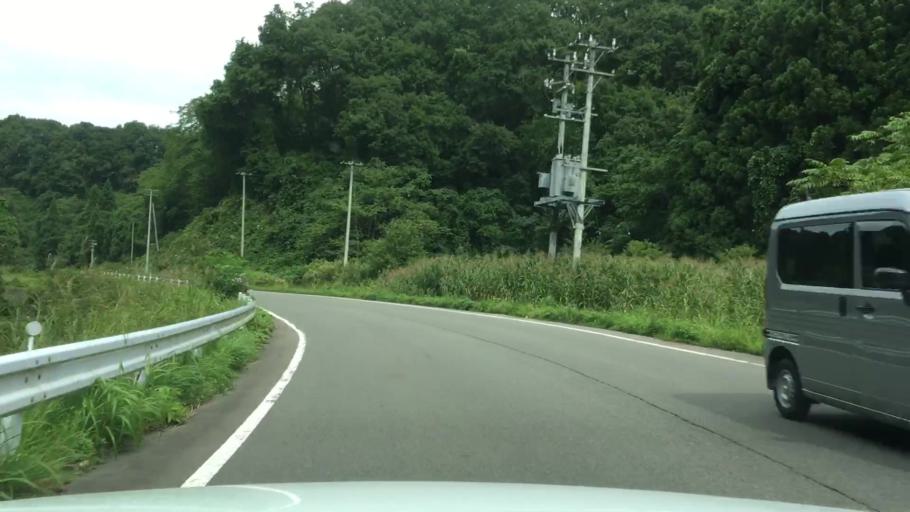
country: JP
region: Aomori
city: Shimokizukuri
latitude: 40.7313
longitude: 140.2521
